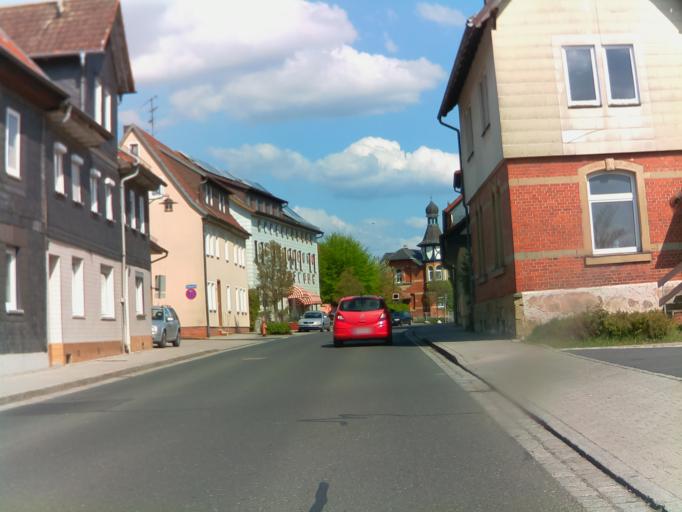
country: DE
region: Thuringia
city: Veilsdorf
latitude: 50.3411
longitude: 10.7823
